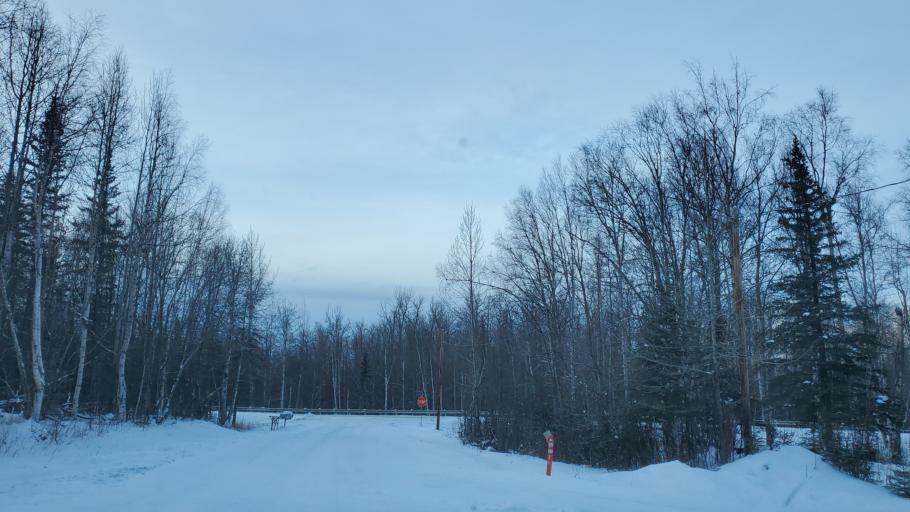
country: US
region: Alaska
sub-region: Matanuska-Susitna Borough
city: Lakes
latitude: 61.6716
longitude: -149.2848
